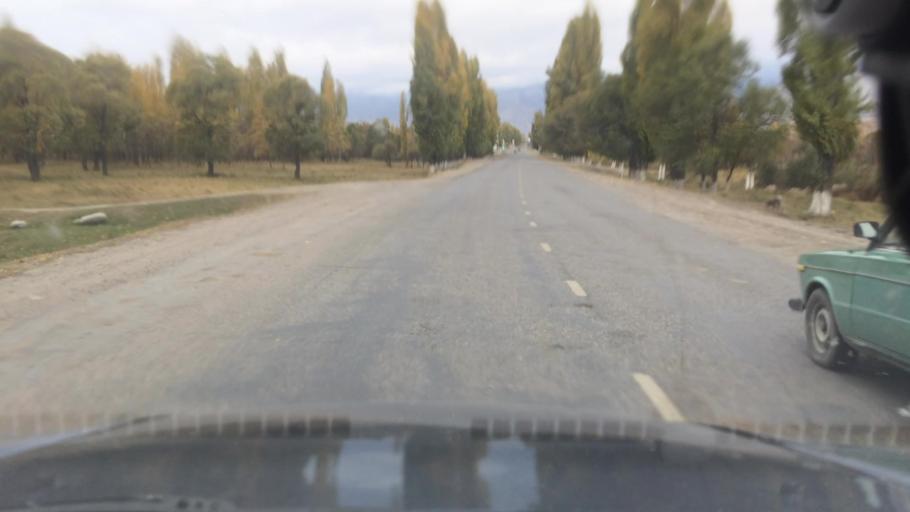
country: KG
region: Ysyk-Koel
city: Tyup
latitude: 42.7351
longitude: 78.3515
